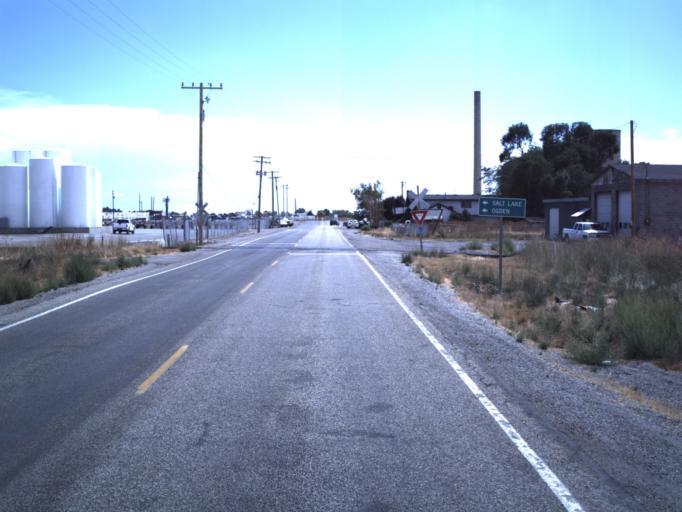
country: US
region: Utah
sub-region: Box Elder County
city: Garland
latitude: 41.7452
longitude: -112.1484
